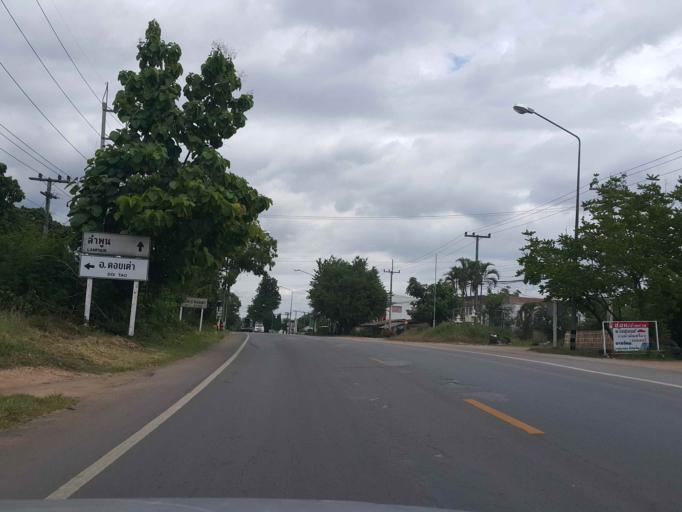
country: TH
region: Lamphun
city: Thung Hua Chang
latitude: 17.9918
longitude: 98.8757
